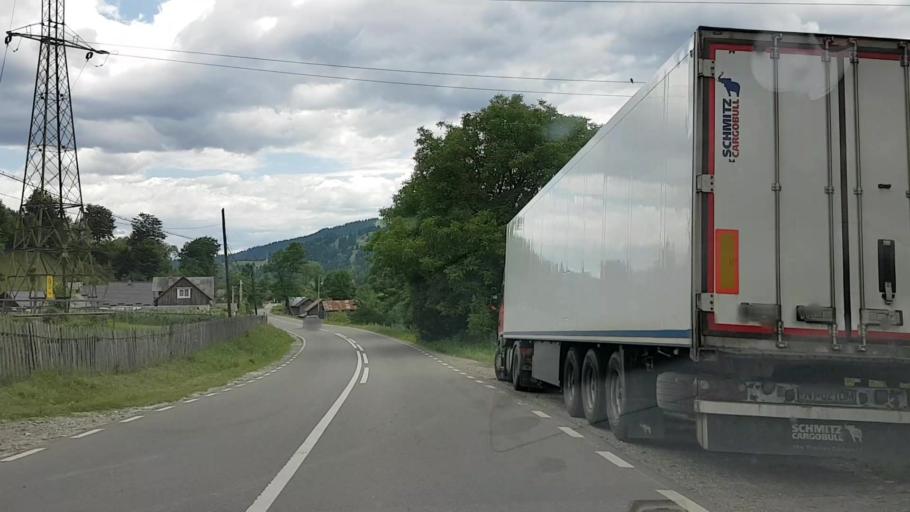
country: RO
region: Neamt
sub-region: Comuna Farcasa
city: Farcasa
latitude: 47.1672
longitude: 25.8049
